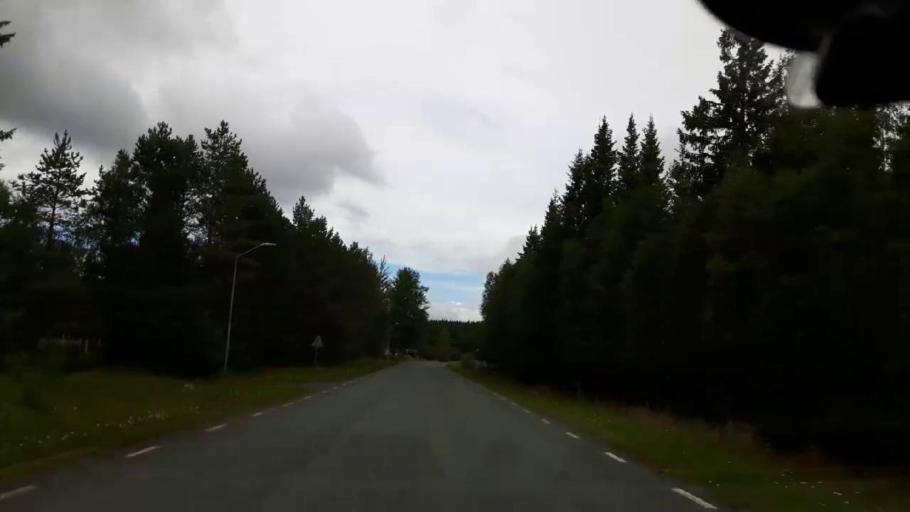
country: SE
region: Jaemtland
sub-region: Krokoms Kommun
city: Valla
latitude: 63.5709
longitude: 13.8371
